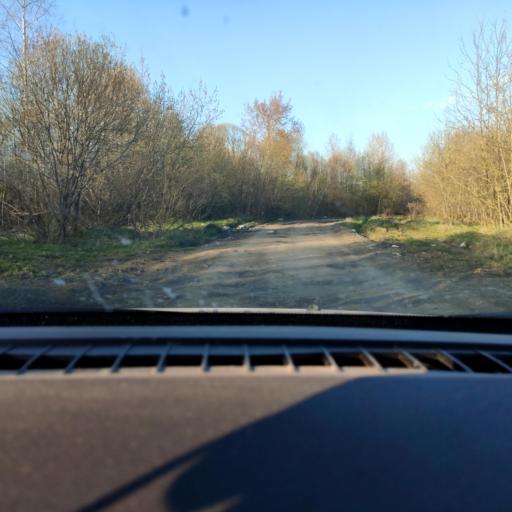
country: RU
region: Perm
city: Perm
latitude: 58.0236
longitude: 56.2081
